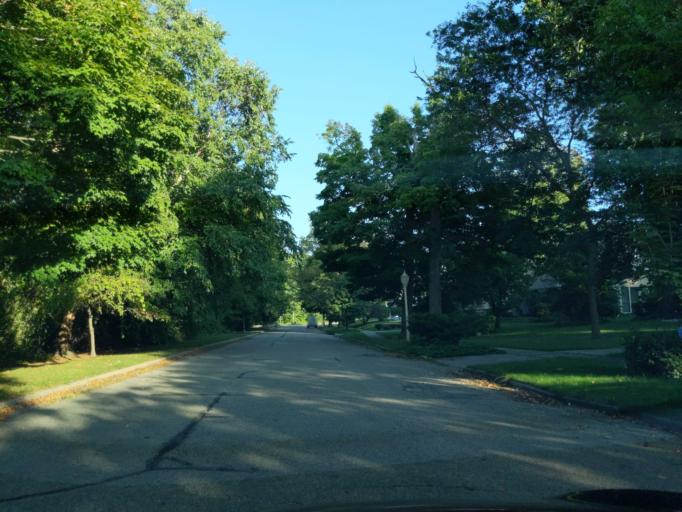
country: US
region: Michigan
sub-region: Ingham County
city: Lansing
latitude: 42.7169
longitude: -84.5341
